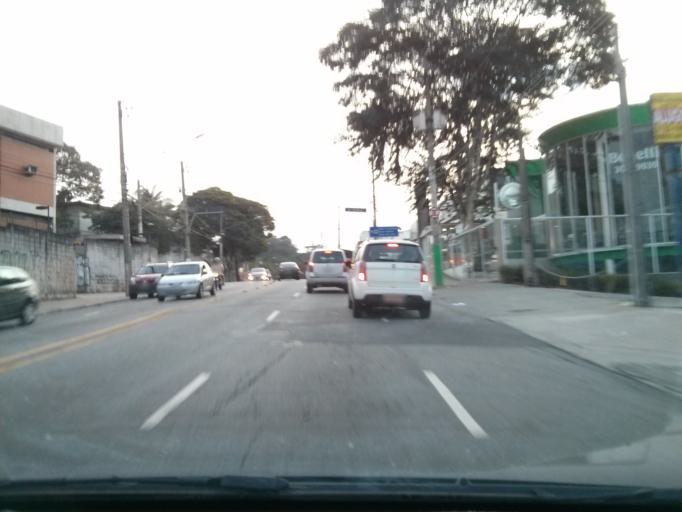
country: BR
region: Sao Paulo
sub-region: Taboao Da Serra
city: Taboao da Serra
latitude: -23.6176
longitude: -46.7040
